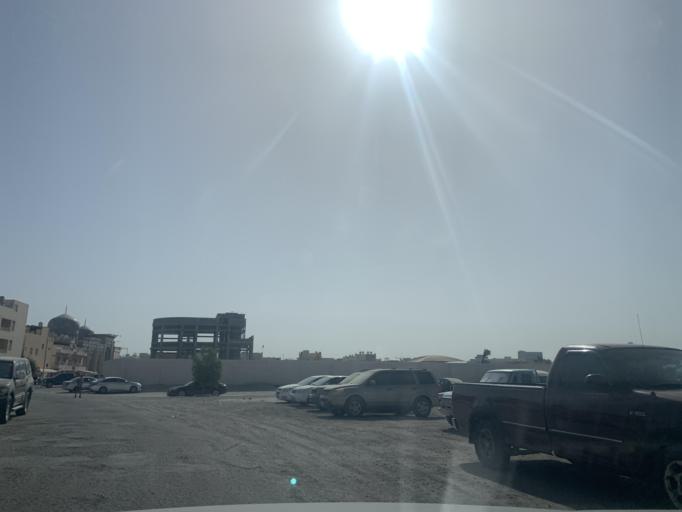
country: BH
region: Manama
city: Jidd Hafs
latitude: 26.2097
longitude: 50.5598
